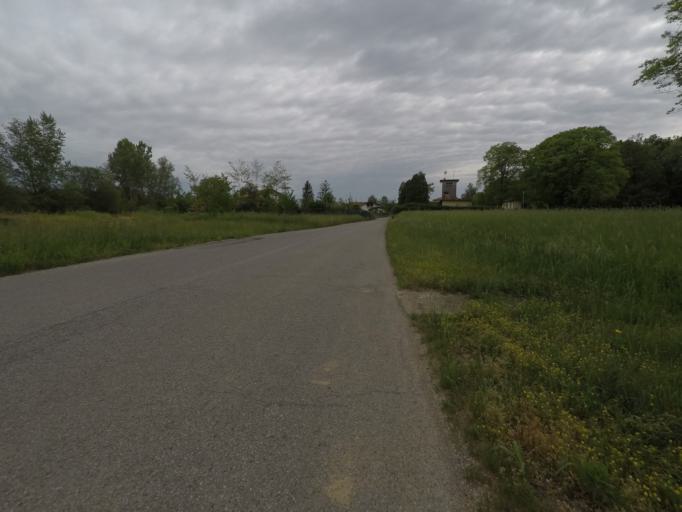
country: IT
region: Friuli Venezia Giulia
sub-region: Provincia di Udine
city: Reana del Rojale
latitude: 46.1730
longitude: 13.2549
